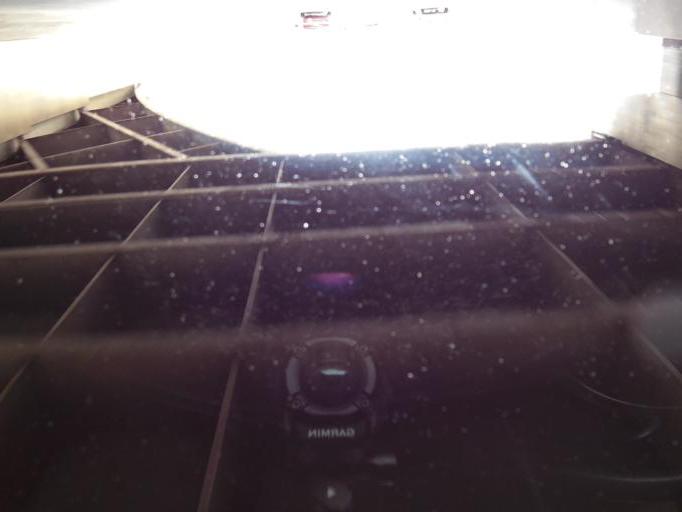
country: US
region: Minnesota
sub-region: Hennepin County
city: Richfield
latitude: 44.8623
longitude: -93.2376
